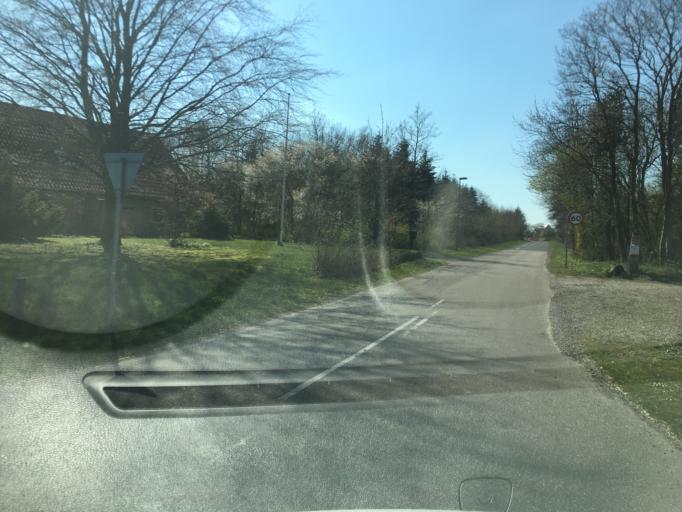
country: DK
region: South Denmark
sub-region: Sonderborg Kommune
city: Grasten
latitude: 54.9283
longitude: 9.4925
